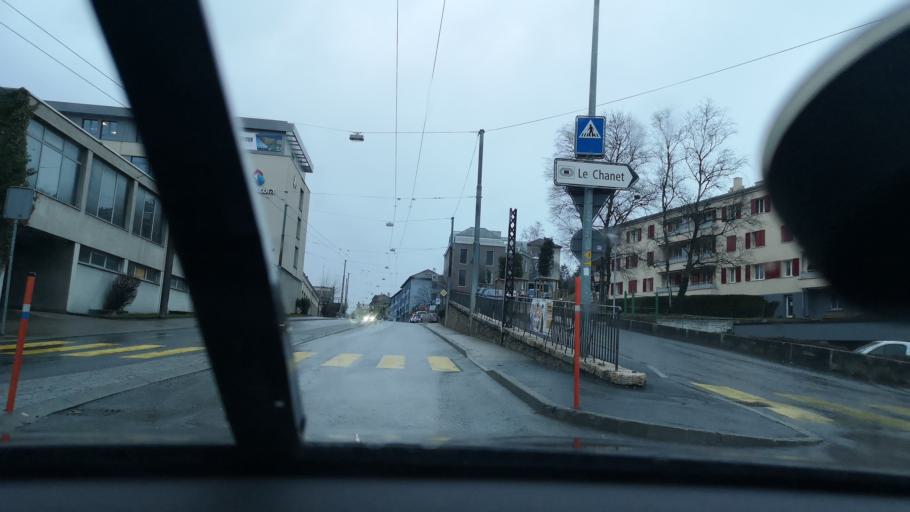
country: CH
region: Neuchatel
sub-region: Boudry District
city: Peseux
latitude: 46.9895
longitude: 6.9058
